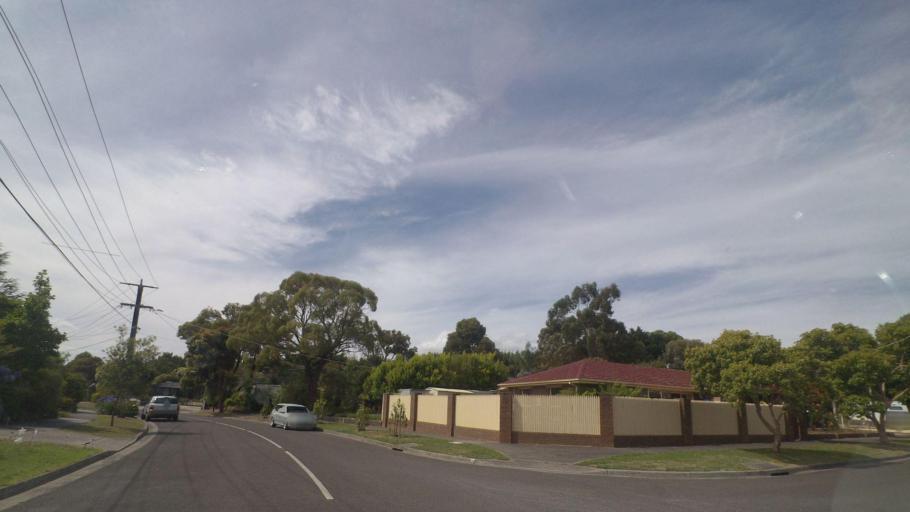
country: AU
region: Victoria
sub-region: Knox
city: The Basin
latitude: -37.8426
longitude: 145.3064
